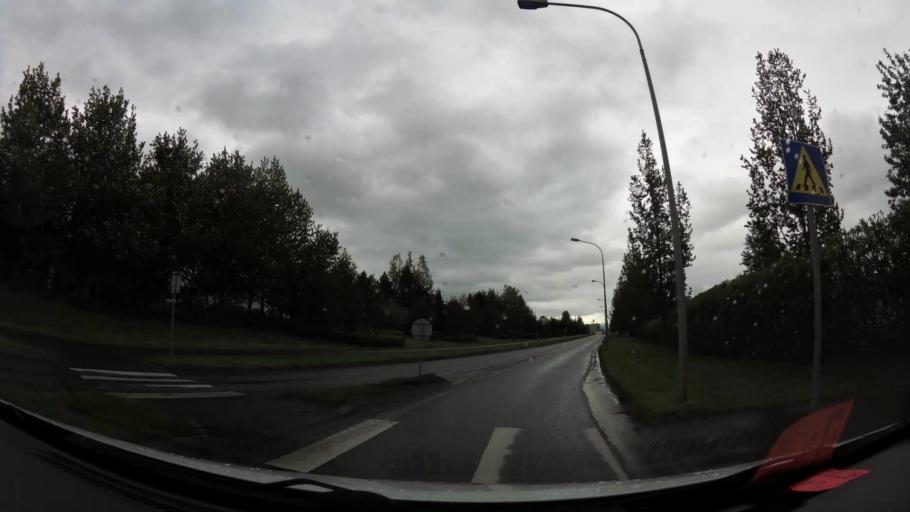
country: IS
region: Northeast
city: Akureyri
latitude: 65.6875
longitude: -18.1292
